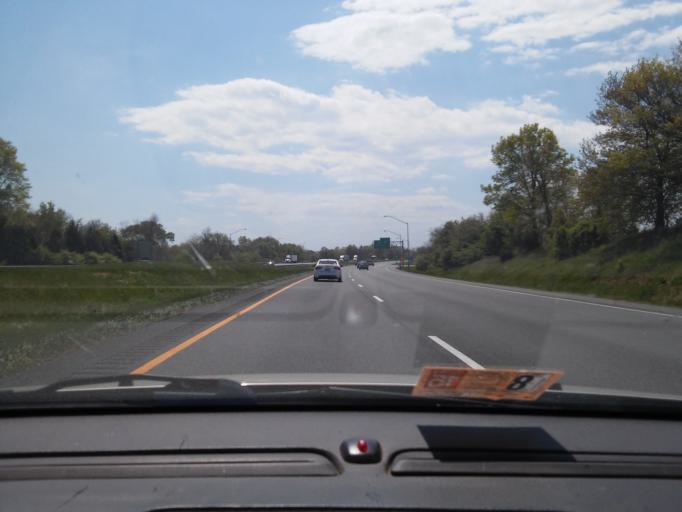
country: US
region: Maryland
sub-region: Washington County
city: Williamsport
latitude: 39.5914
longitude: -77.8114
